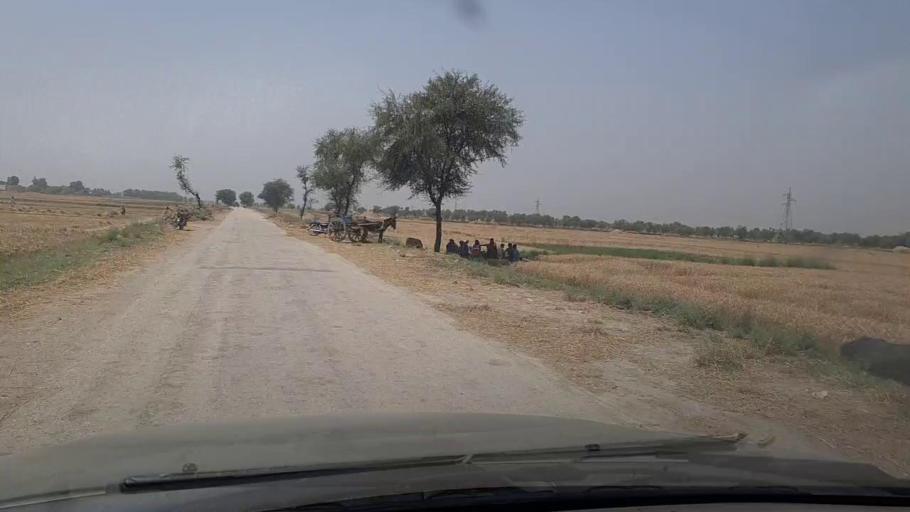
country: PK
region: Sindh
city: Ratodero
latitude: 27.7955
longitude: 68.2487
